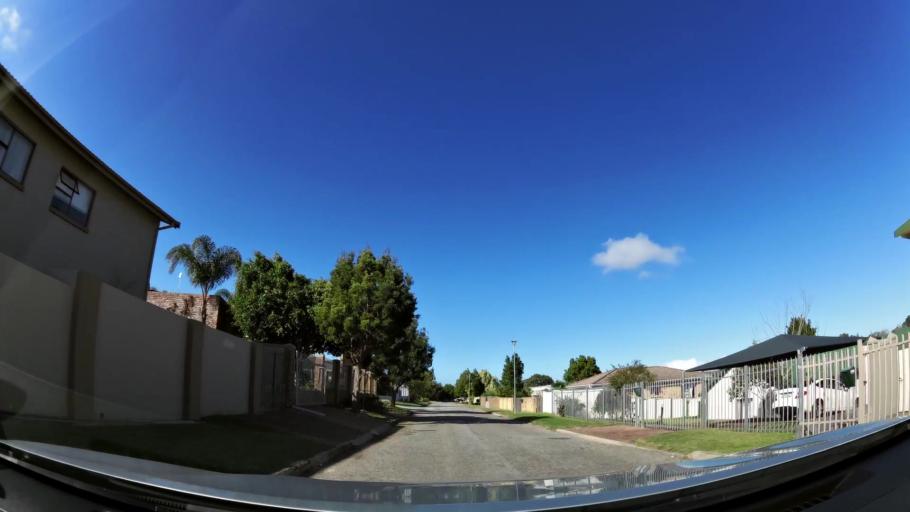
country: ZA
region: Western Cape
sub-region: Eden District Municipality
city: George
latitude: -33.9678
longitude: 22.4948
